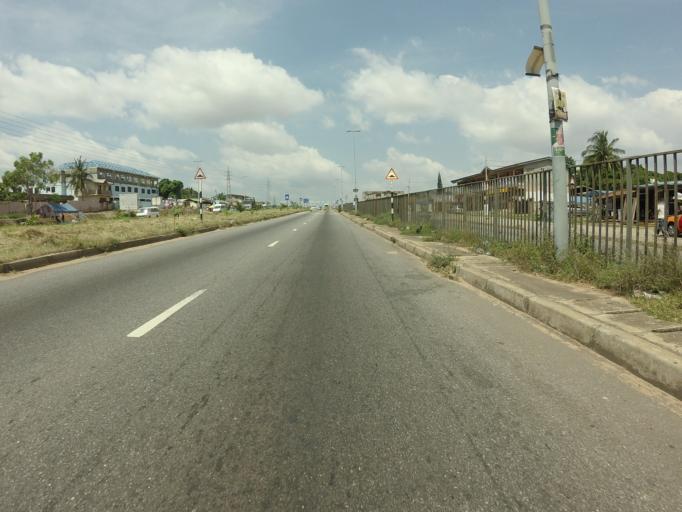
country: GH
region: Greater Accra
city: Gbawe
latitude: 5.5965
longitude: -0.2898
